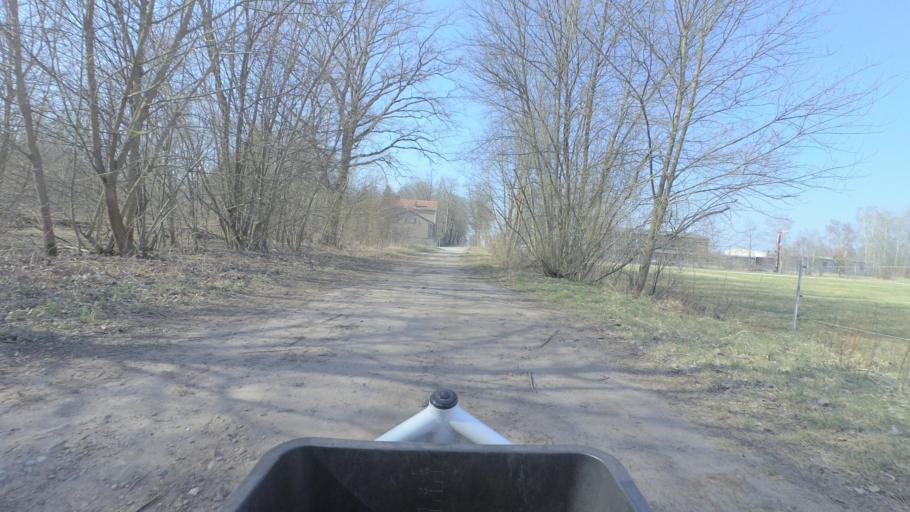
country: DE
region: Brandenburg
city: Sperenberg
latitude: 52.1598
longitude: 13.3767
